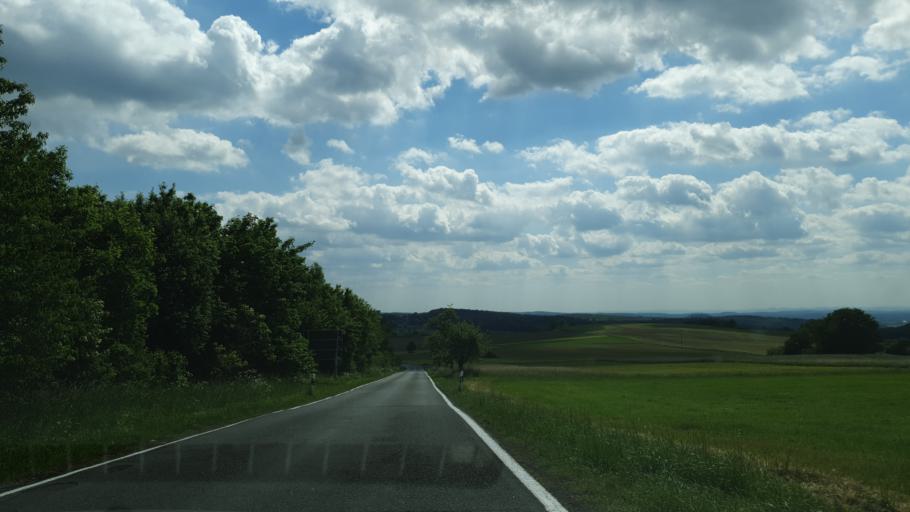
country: DE
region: Rheinland-Pfalz
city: Wolferlingen
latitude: 50.5549
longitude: 7.8482
